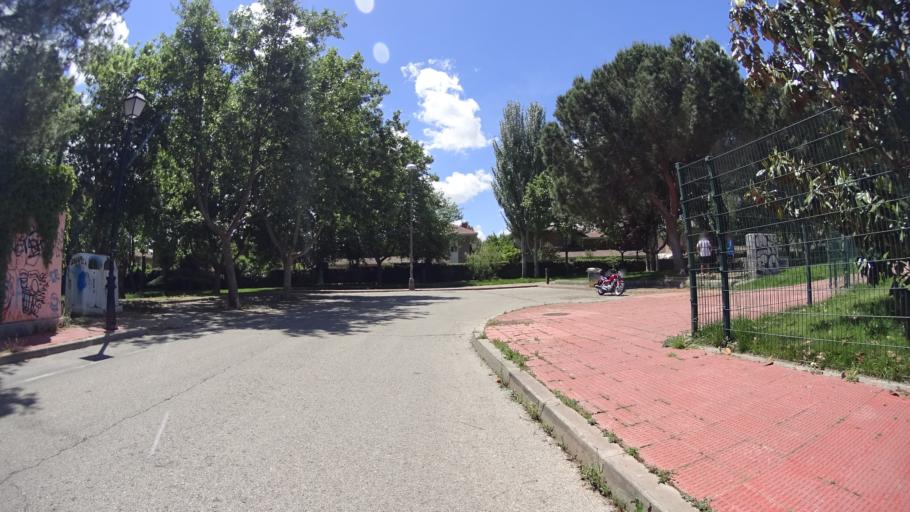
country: ES
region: Madrid
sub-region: Provincia de Madrid
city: Villanueva del Pardillo
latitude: 40.4650
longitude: -3.9473
